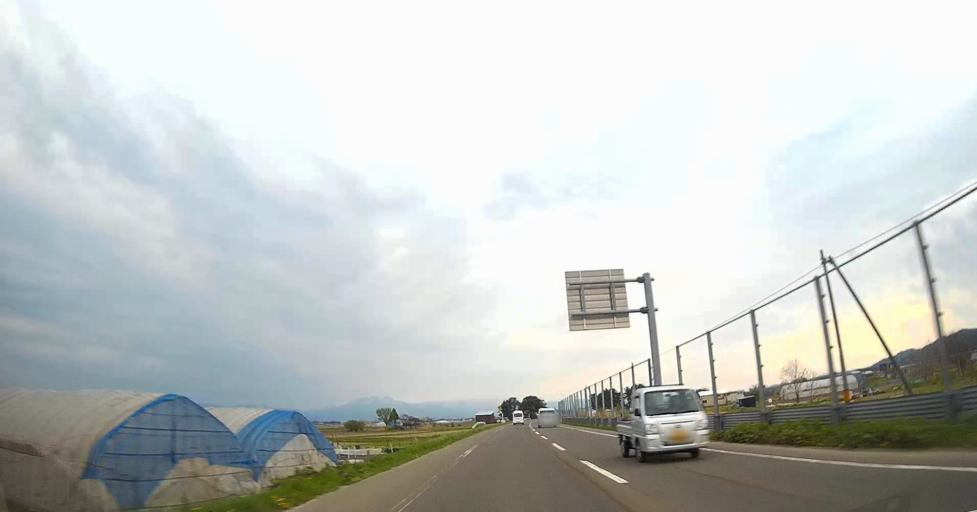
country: JP
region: Aomori
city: Aomori Shi
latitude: 40.9005
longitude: 140.6670
